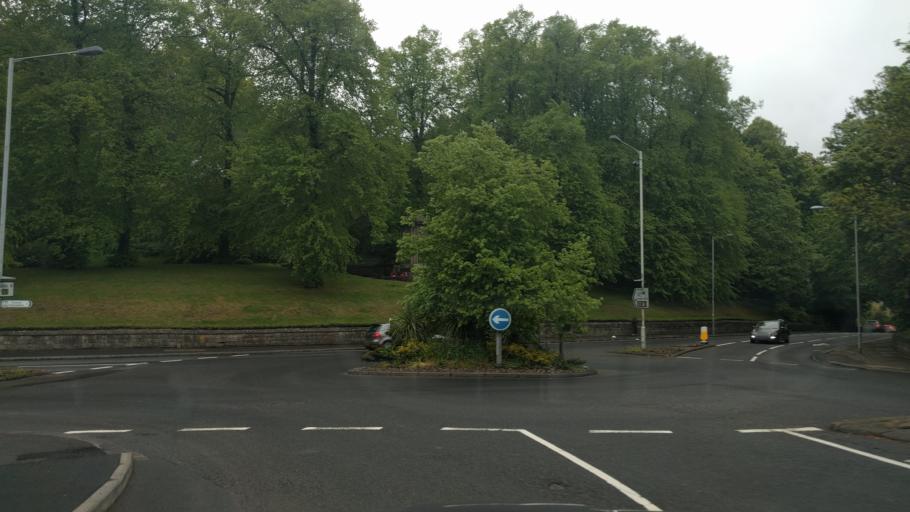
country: GB
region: England
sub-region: Northumberland
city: Morpeth
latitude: 55.1631
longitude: -1.6849
